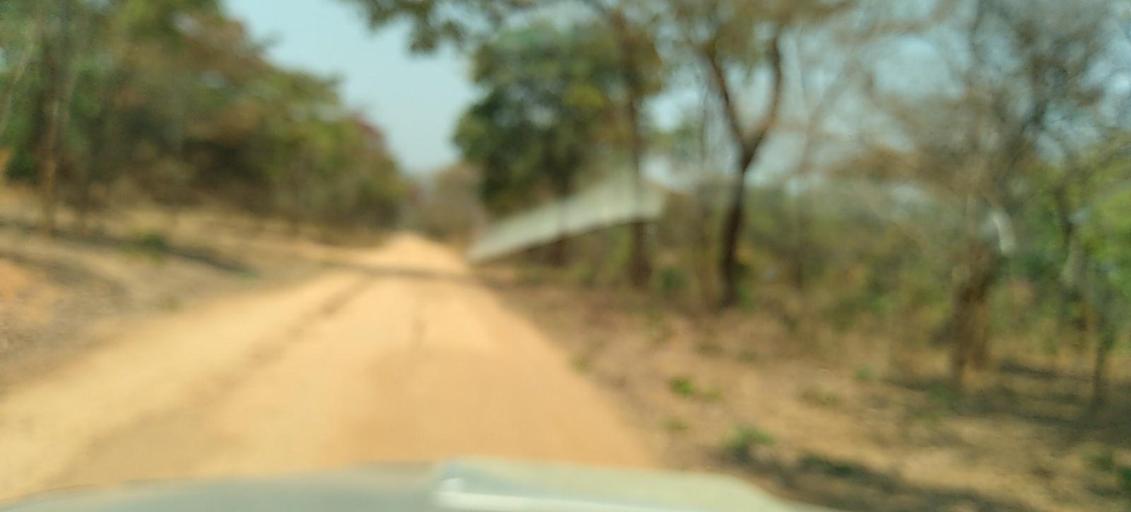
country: ZM
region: North-Western
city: Kasempa
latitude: -13.6661
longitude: 26.2850
